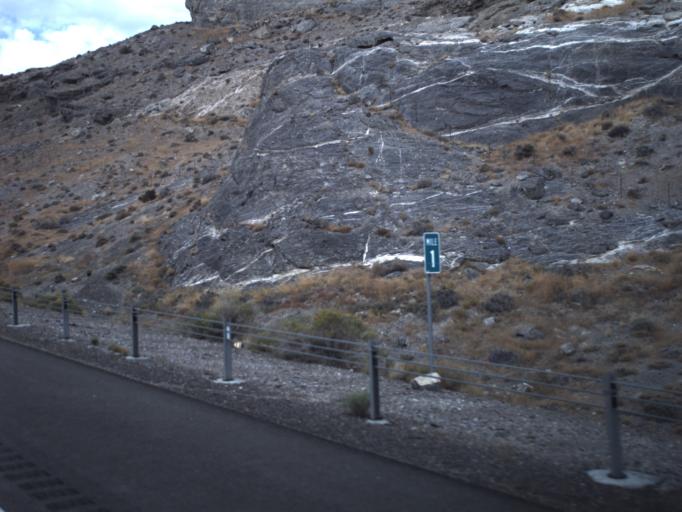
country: US
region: Utah
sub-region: Tooele County
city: Wendover
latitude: 40.7436
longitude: -114.0260
